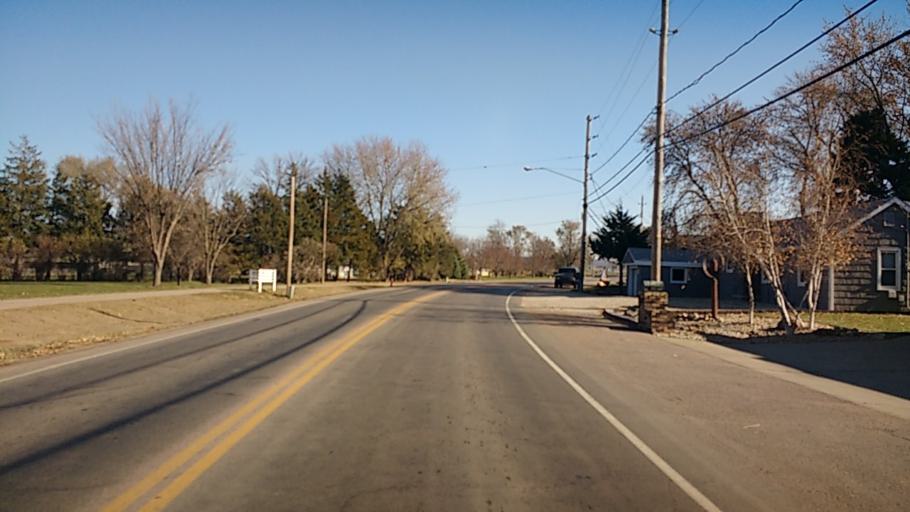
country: US
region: South Dakota
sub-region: Union County
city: North Sioux City
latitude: 42.5510
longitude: -96.5148
